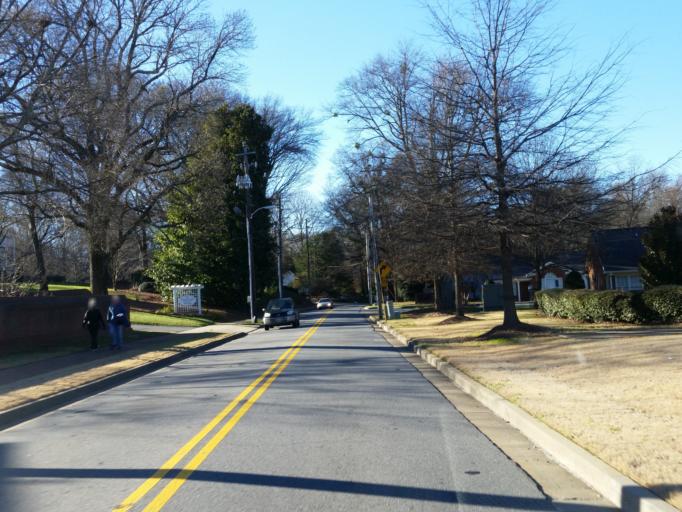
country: US
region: Georgia
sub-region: Cobb County
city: Marietta
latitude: 33.9642
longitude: -84.5587
